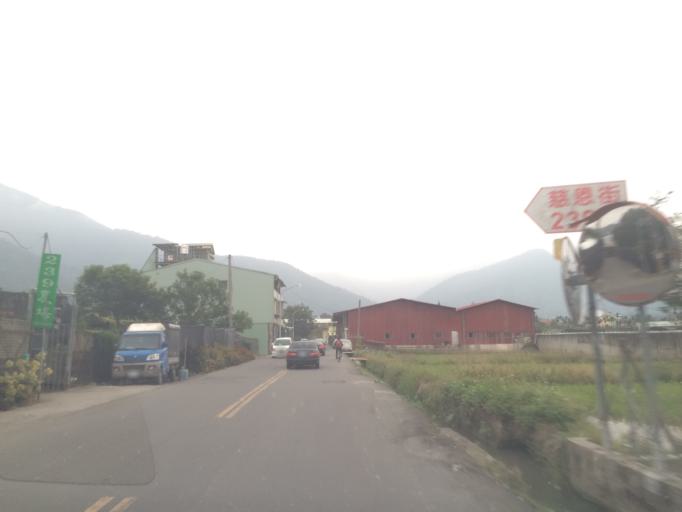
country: TW
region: Taiwan
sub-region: Nantou
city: Puli
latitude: 23.9541
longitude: 120.9792
